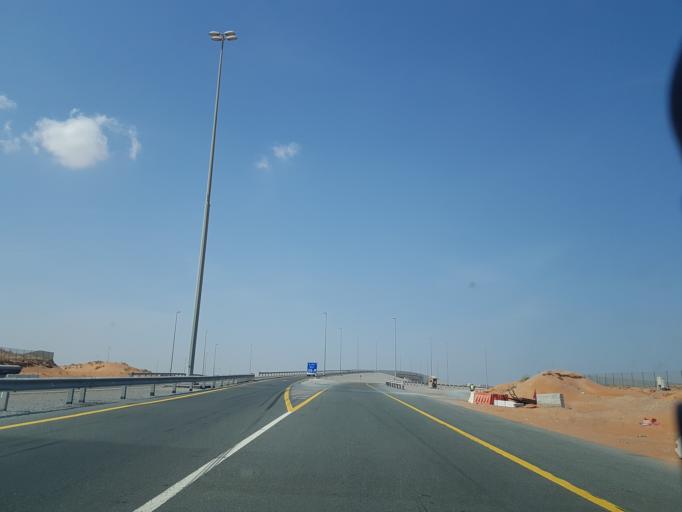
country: AE
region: Ra's al Khaymah
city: Ras al-Khaimah
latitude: 25.6707
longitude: 55.8839
